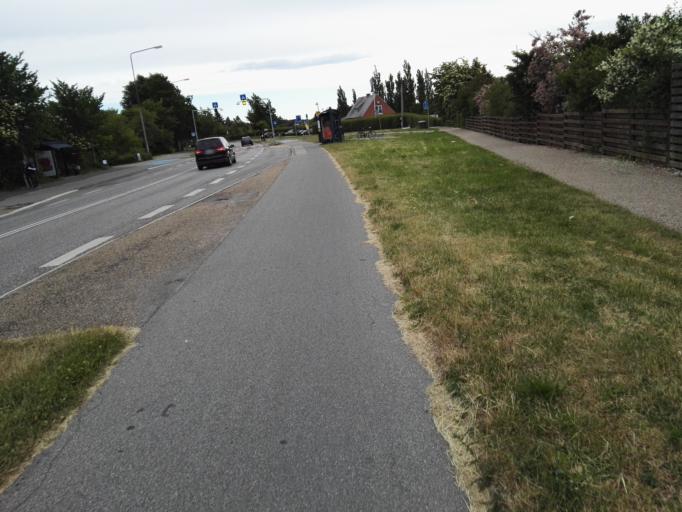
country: DK
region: Capital Region
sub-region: Ballerup Kommune
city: Ballerup
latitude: 55.7419
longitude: 12.3669
